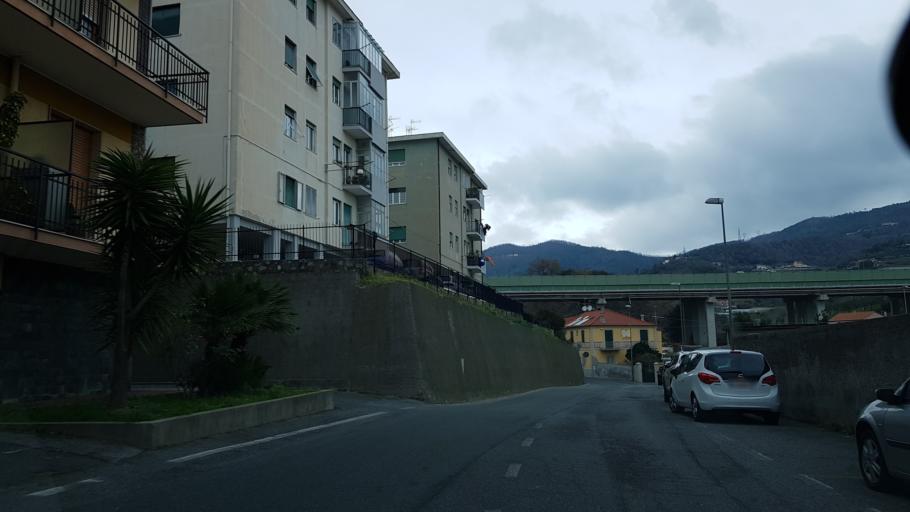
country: IT
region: Liguria
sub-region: Provincia di Savona
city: Savona
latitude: 44.3013
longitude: 8.4499
